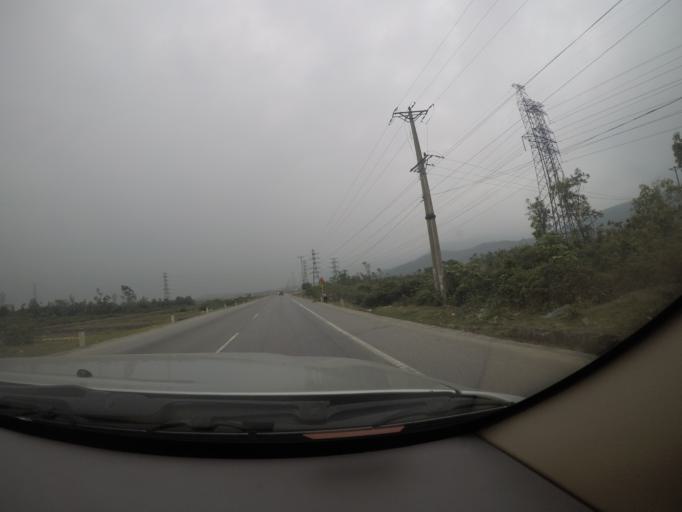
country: VN
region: Ha Tinh
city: Ky Anh
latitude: 18.0060
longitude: 106.4224
